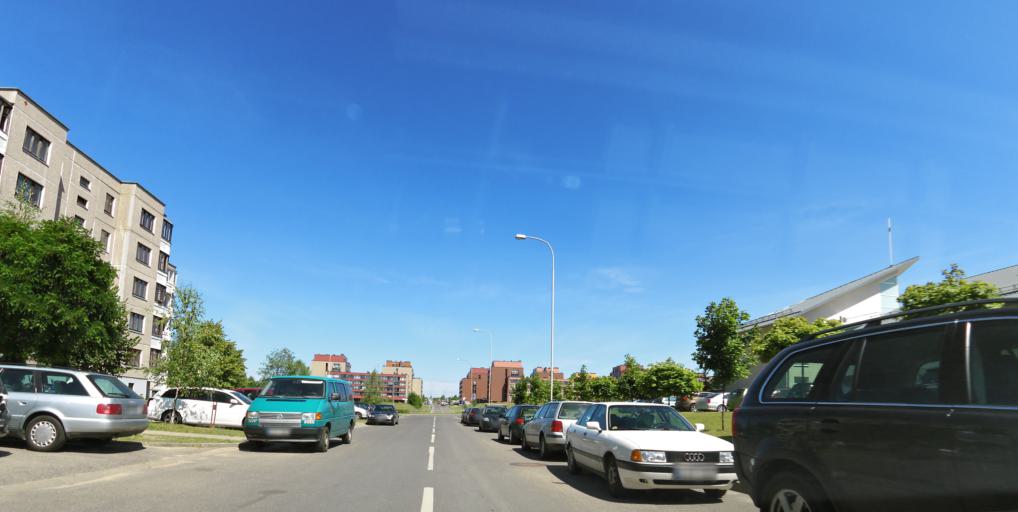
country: LT
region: Vilnius County
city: Pilaite
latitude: 54.7091
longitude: 25.1797
